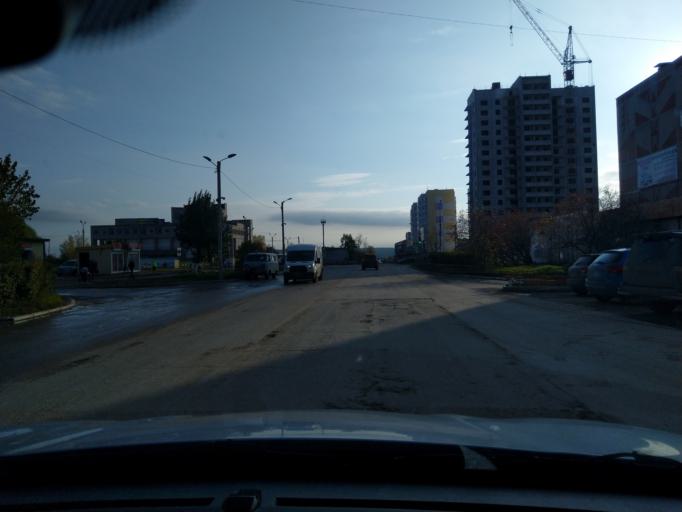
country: RU
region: Perm
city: Dobryanka
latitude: 58.4638
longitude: 56.4006
